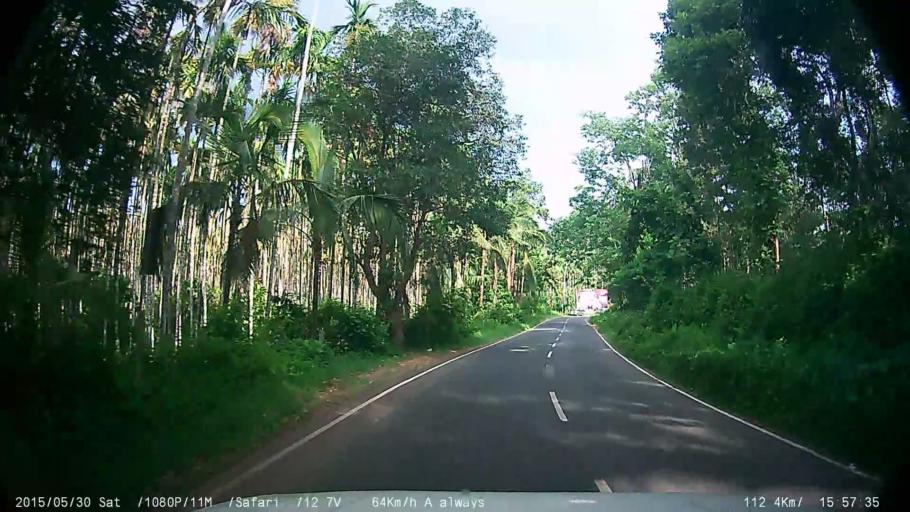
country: IN
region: Kerala
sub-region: Wayanad
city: Kalpetta
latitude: 11.6545
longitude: 76.0877
